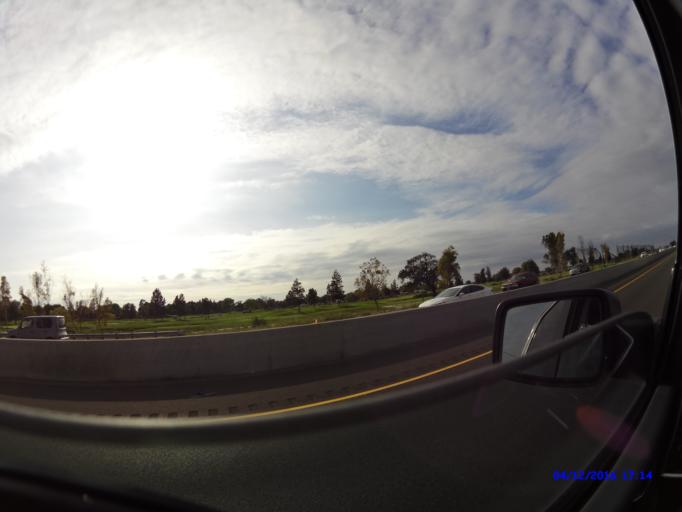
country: US
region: California
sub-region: San Joaquin County
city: French Camp
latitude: 37.8662
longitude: -121.2189
